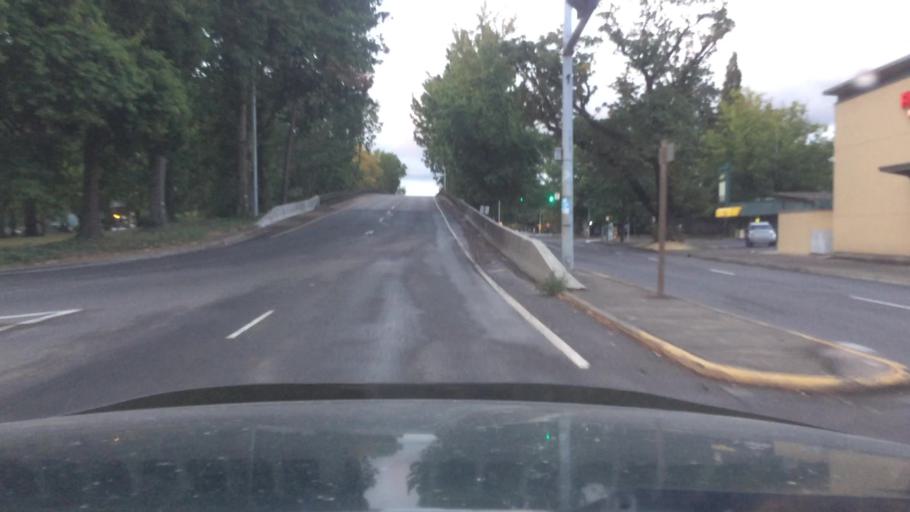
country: US
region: Oregon
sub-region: Lane County
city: Eugene
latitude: 44.0522
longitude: -123.1004
